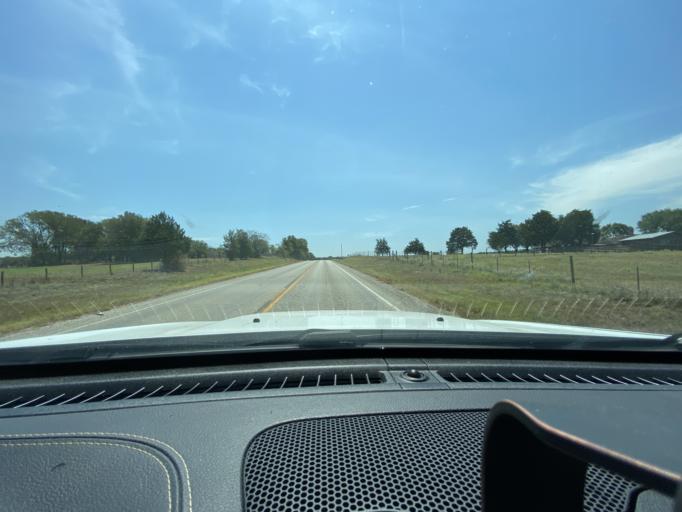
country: US
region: Texas
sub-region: Lee County
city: Giddings
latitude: 30.1220
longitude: -96.9915
